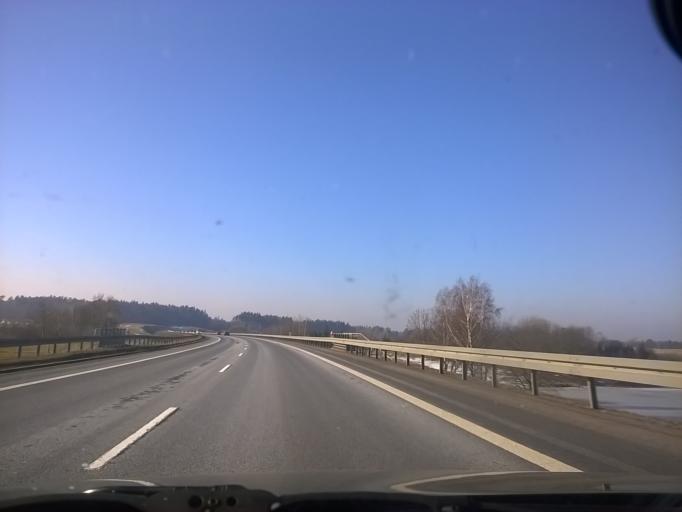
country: PL
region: Warmian-Masurian Voivodeship
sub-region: Powiat olsztynski
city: Barczewo
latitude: 53.8286
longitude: 20.7930
